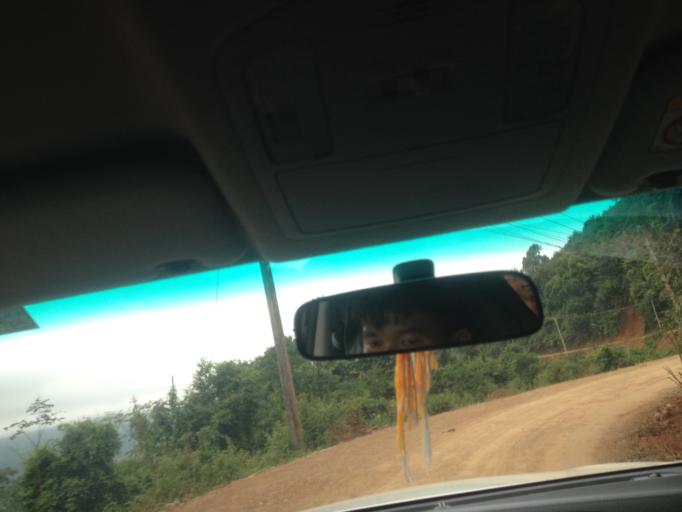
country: TH
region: Nan
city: Chaloem Phra Kiat
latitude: 19.9909
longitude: 101.1404
